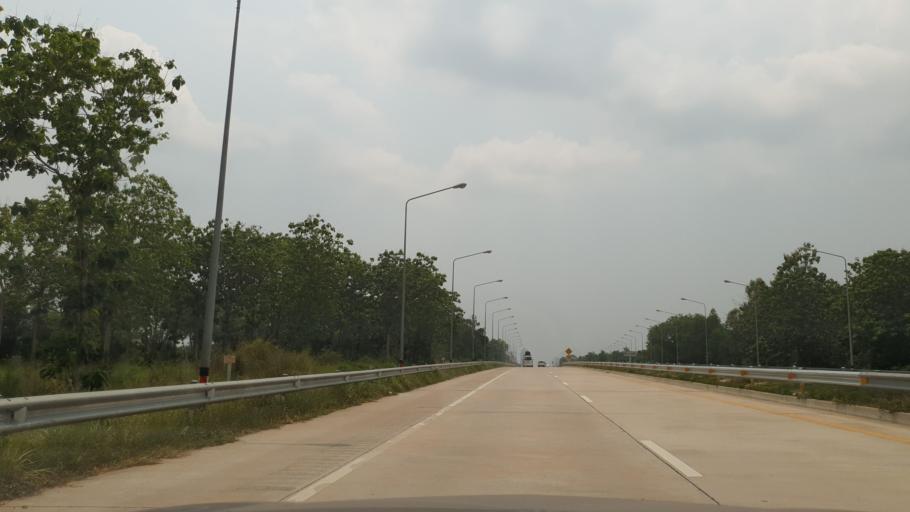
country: TH
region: Chon Buri
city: Phatthaya
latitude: 12.8399
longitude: 100.9527
